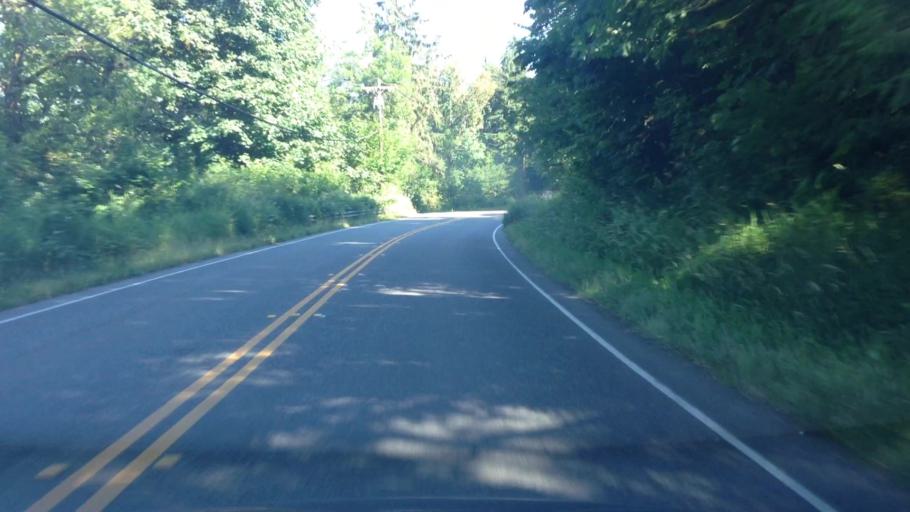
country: US
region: Washington
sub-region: King County
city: Duvall
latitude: 47.7483
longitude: -121.9622
